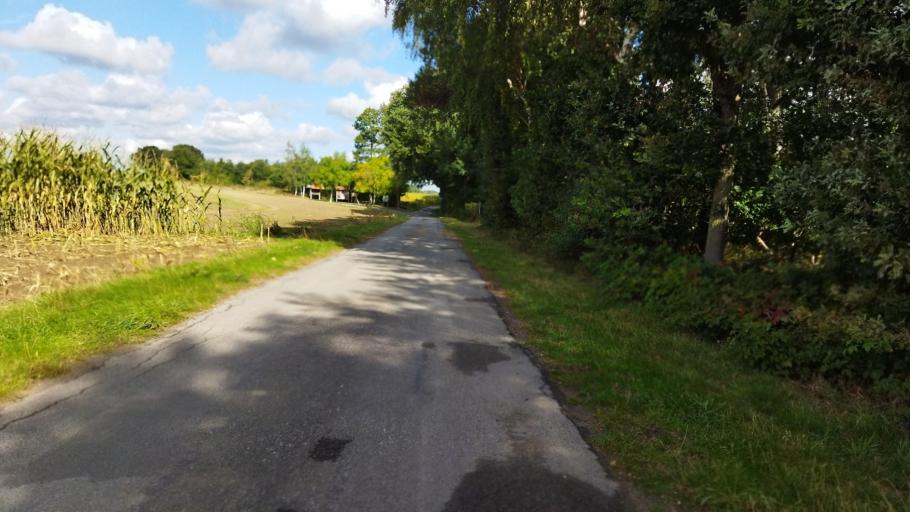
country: DE
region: Lower Saxony
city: Salzbergen
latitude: 52.3632
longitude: 7.3347
